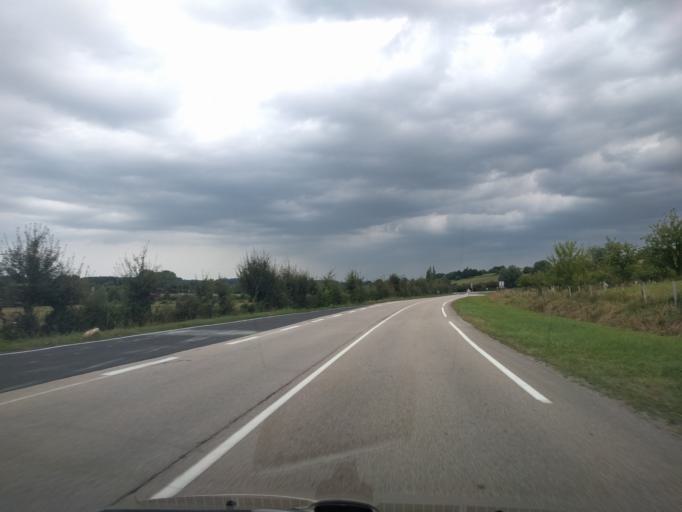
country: FR
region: Lower Normandy
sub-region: Departement de l'Orne
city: Gace
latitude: 48.7754
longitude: 0.3028
